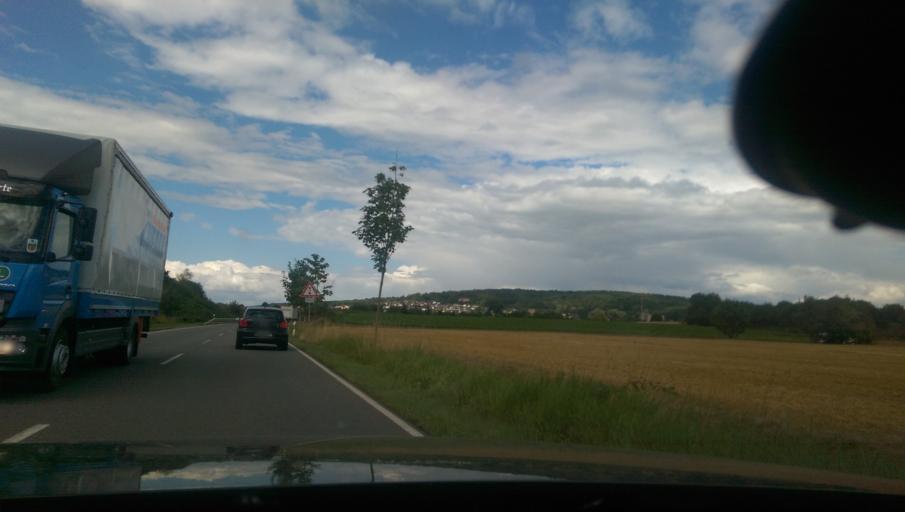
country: DE
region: Lower Saxony
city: Northeim
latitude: 51.7081
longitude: 9.9781
